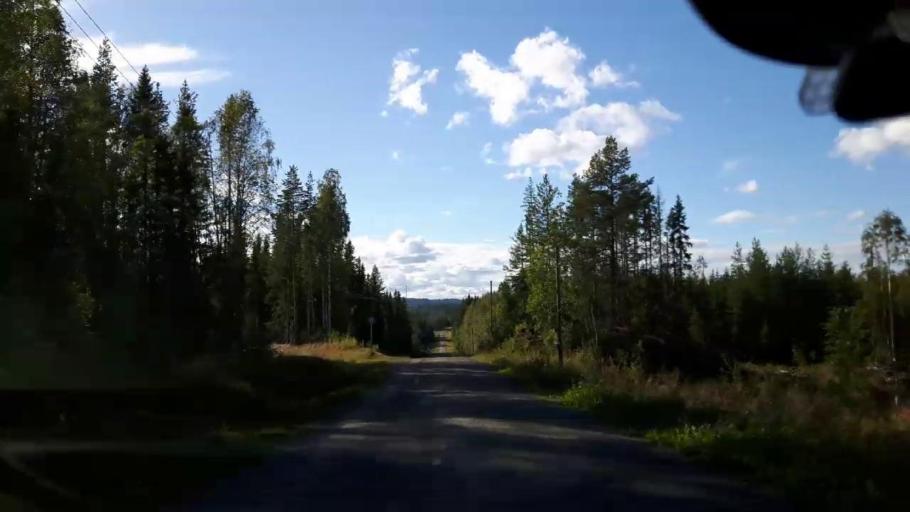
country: SE
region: Vaesternorrland
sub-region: Solleftea Kommun
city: As
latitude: 63.4630
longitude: 16.2481
